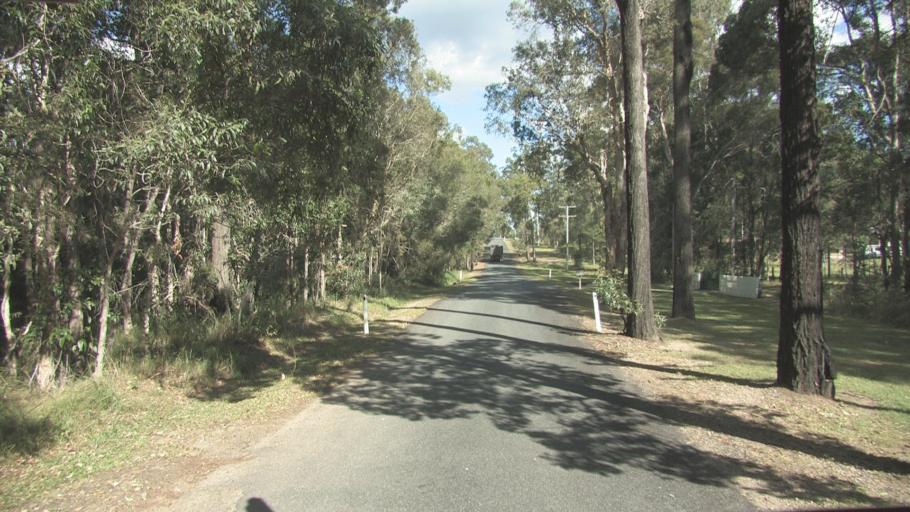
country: AU
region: Queensland
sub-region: Logan
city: Beenleigh
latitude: -27.6488
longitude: 153.2281
